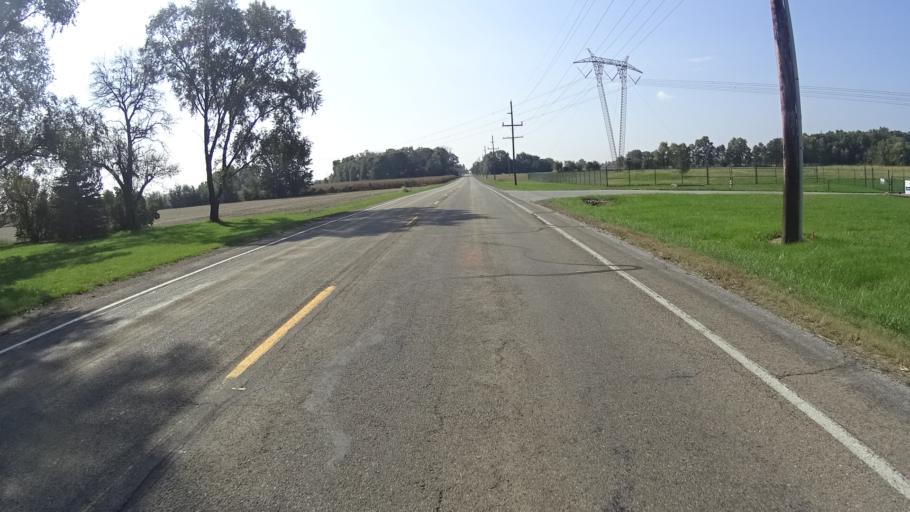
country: US
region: Indiana
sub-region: Madison County
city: Lapel
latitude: 40.0271
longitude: -85.8433
